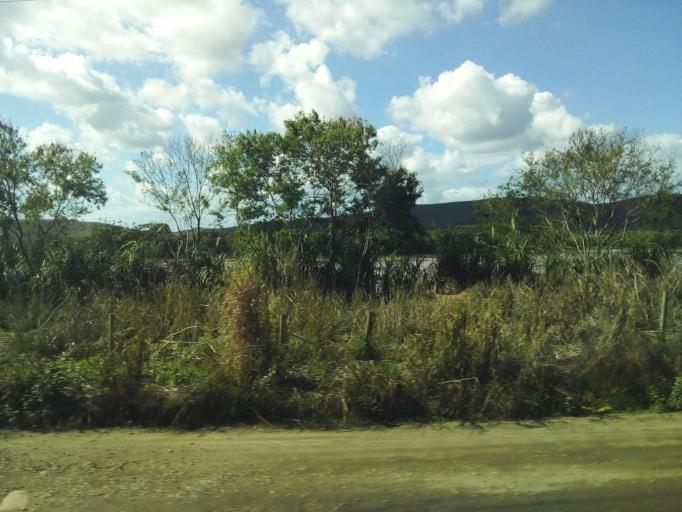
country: BR
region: Minas Gerais
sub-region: Governador Valadares
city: Governador Valadares
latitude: -18.8686
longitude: -41.7724
